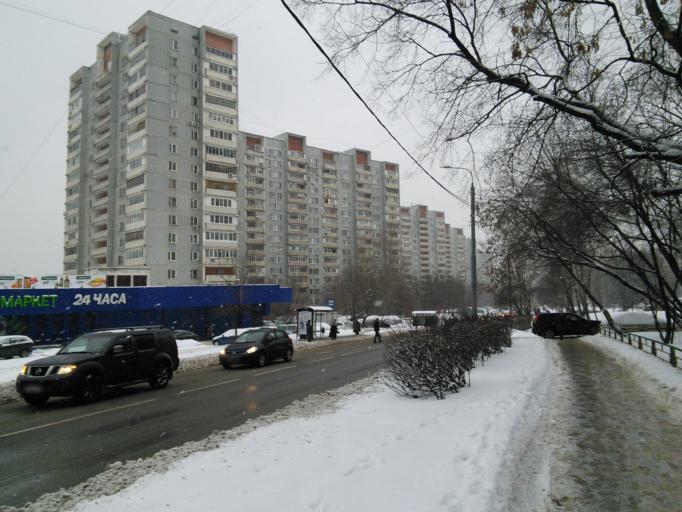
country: RU
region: Moscow
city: Vatutino
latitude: 55.8875
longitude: 37.6551
